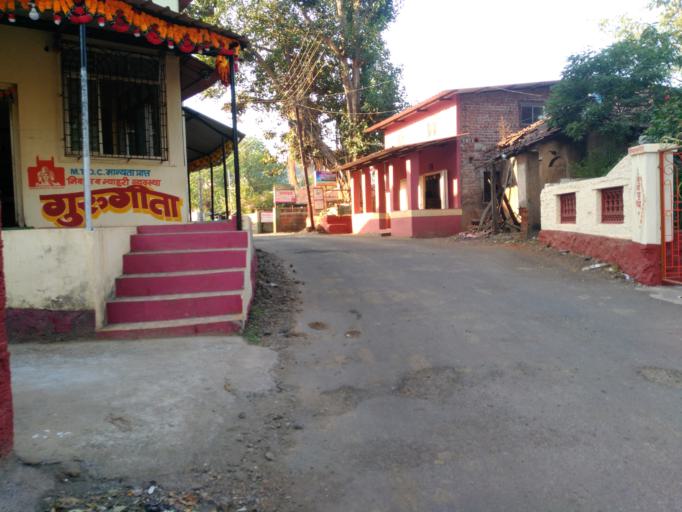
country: IN
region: Maharashtra
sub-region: Raigarh
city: Srivardhan
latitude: 17.9952
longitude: 73.0228
